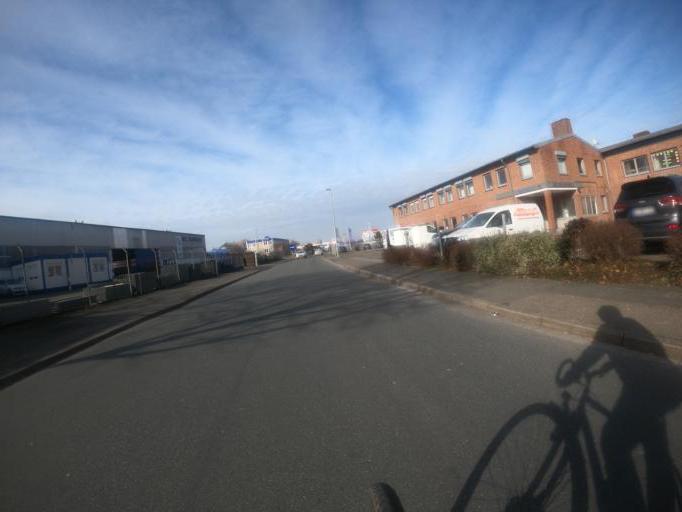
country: DE
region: Lower Saxony
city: Lueneburg
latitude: 53.2712
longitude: 10.4109
